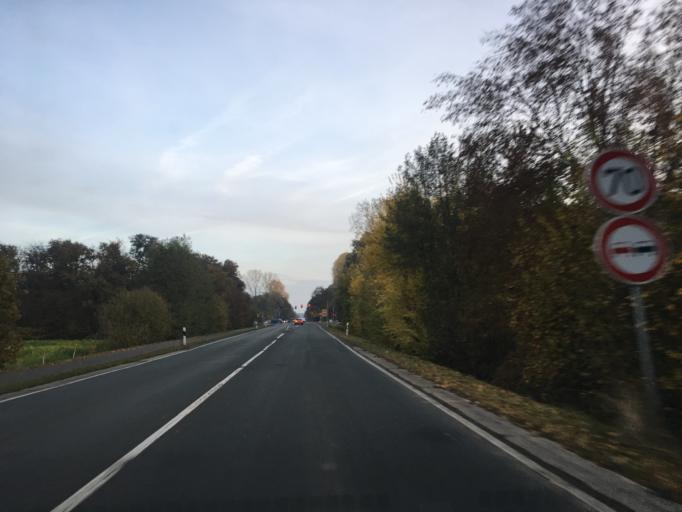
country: DE
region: North Rhine-Westphalia
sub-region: Regierungsbezirk Munster
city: Altenberge
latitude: 52.0741
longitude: 7.4354
